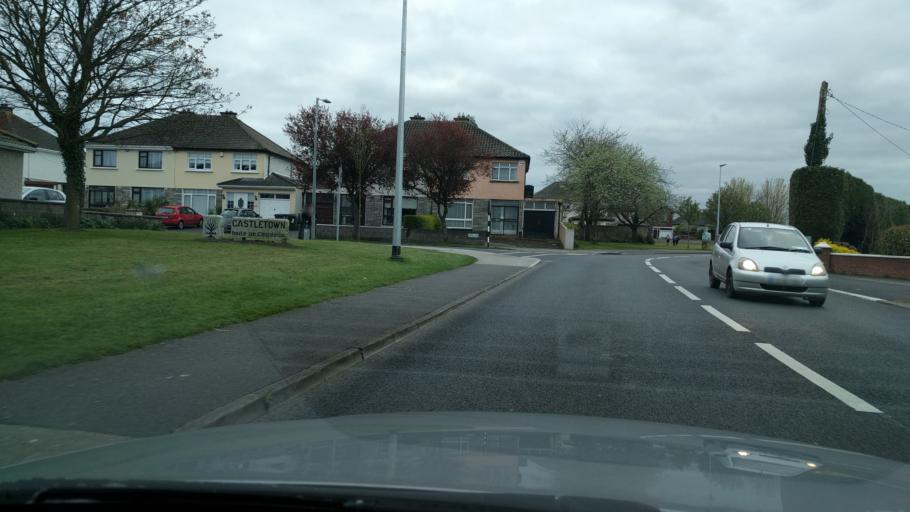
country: IE
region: Leinster
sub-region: Kildare
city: Leixlip
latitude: 53.3652
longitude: -6.5056
